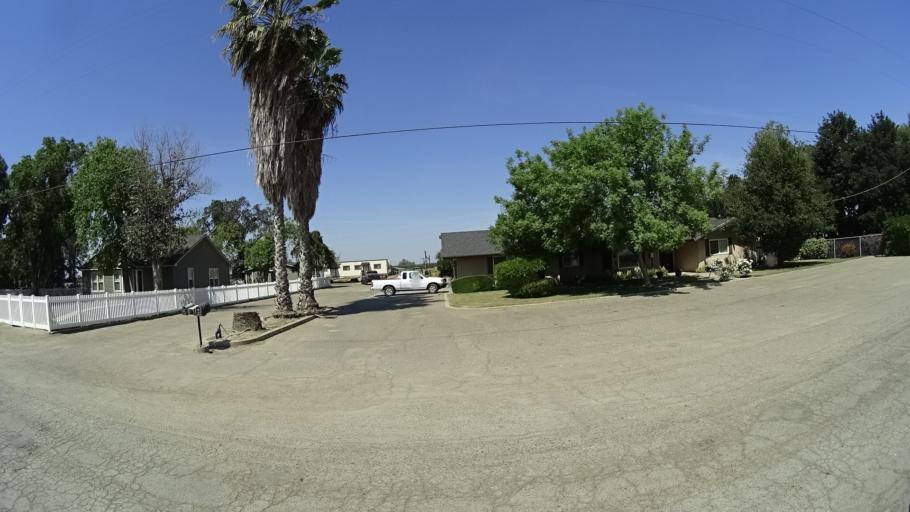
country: US
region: California
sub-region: Fresno County
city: Riverdale
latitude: 36.3943
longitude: -119.8872
